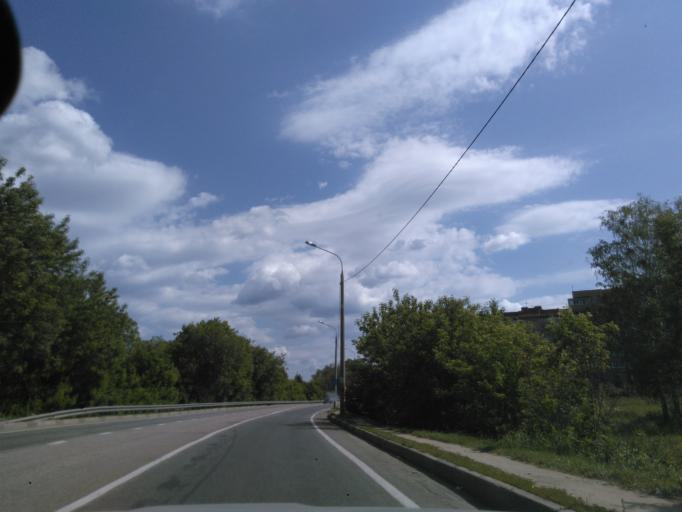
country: RU
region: Moskovskaya
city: Solnechnogorsk
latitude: 56.1886
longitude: 36.9659
